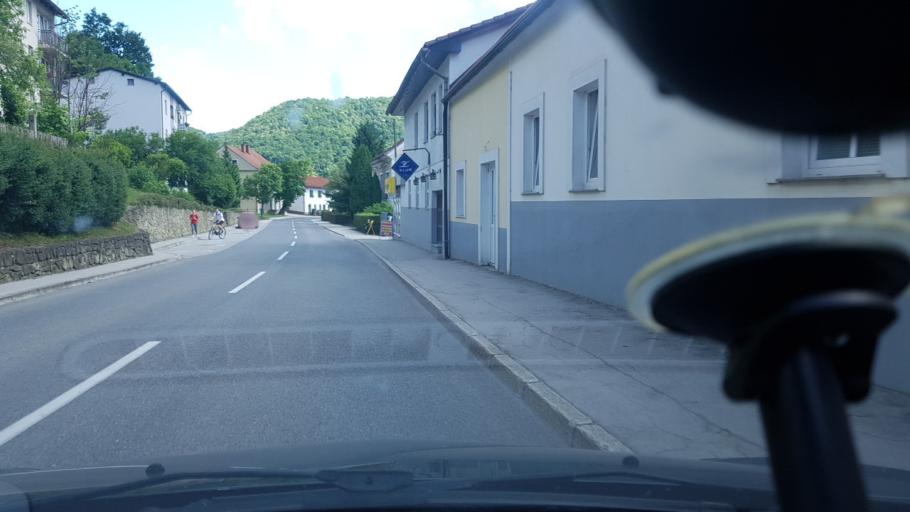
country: SI
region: Rogatec
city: Rogatec
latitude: 46.2276
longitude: 15.6994
